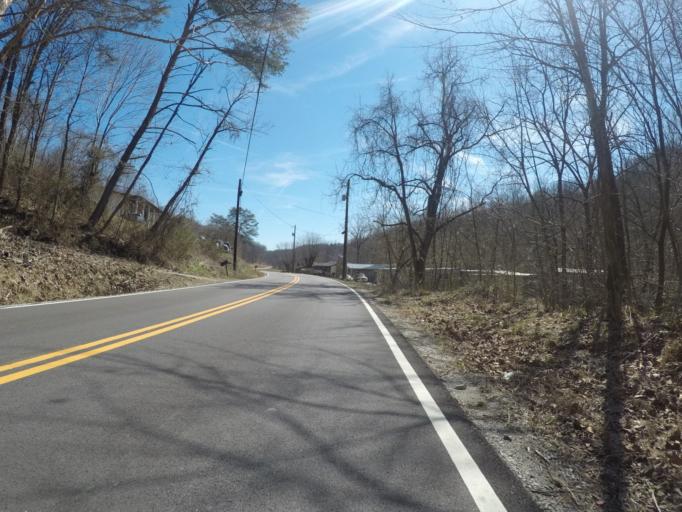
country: US
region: Ohio
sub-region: Lawrence County
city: Burlington
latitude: 38.4567
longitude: -82.5239
